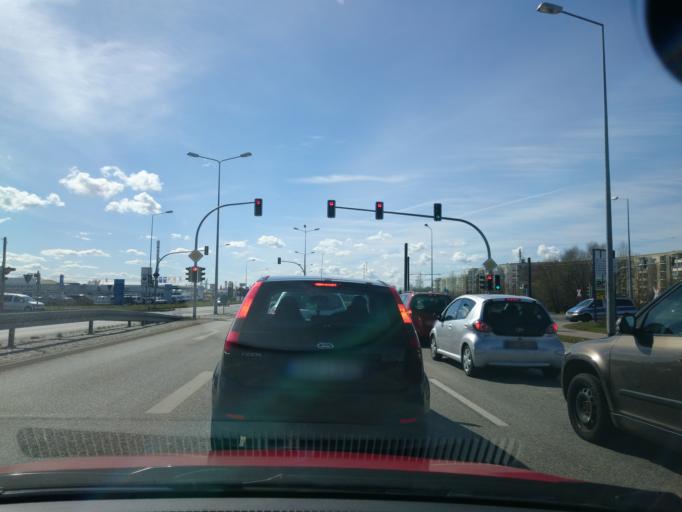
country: DE
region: Mecklenburg-Vorpommern
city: Dierkow-Neu
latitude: 54.1026
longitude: 12.1816
